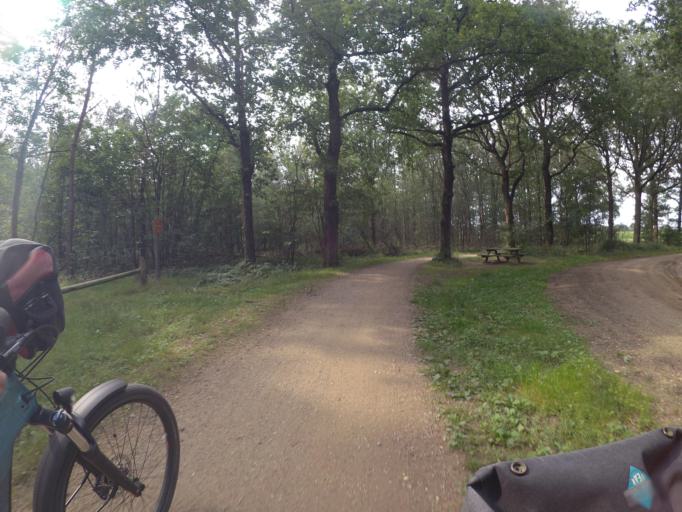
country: NL
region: Limburg
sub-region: Gemeente Gennep
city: Gennep
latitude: 51.6534
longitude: 6.0458
